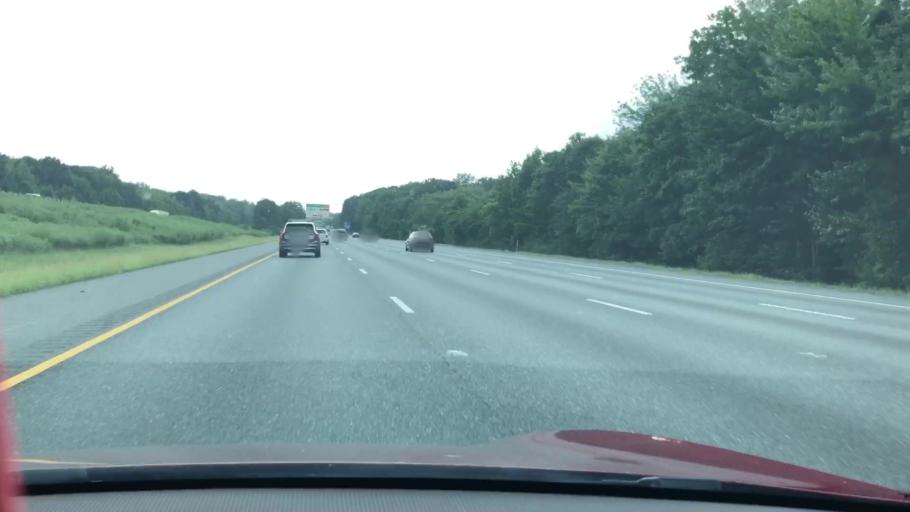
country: US
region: Maryland
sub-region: Baltimore County
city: White Marsh
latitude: 39.4061
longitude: -76.4203
